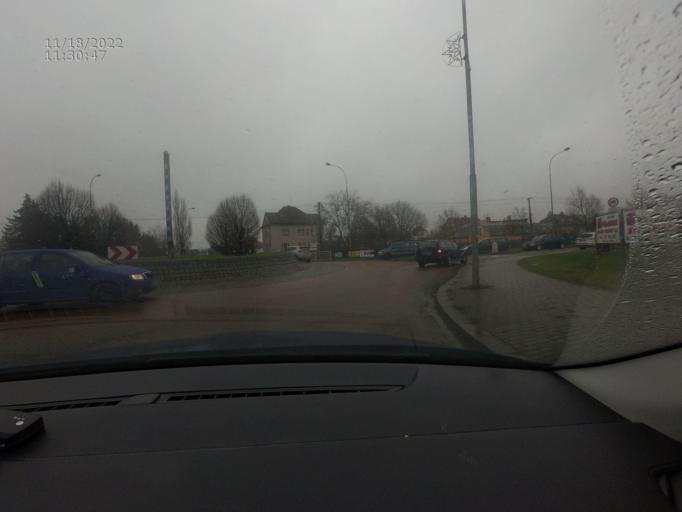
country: CZ
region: Plzensky
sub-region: Okres Rokycany
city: Rokycany
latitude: 49.7421
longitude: 13.5815
